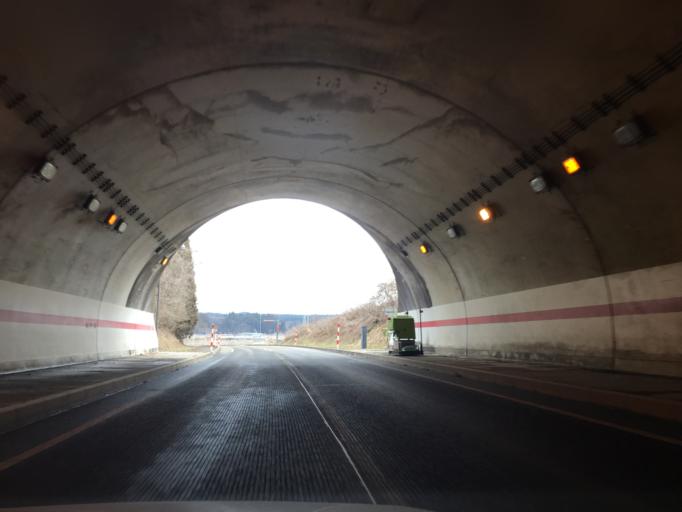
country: JP
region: Akita
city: Takanosu
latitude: 40.1906
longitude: 140.3879
